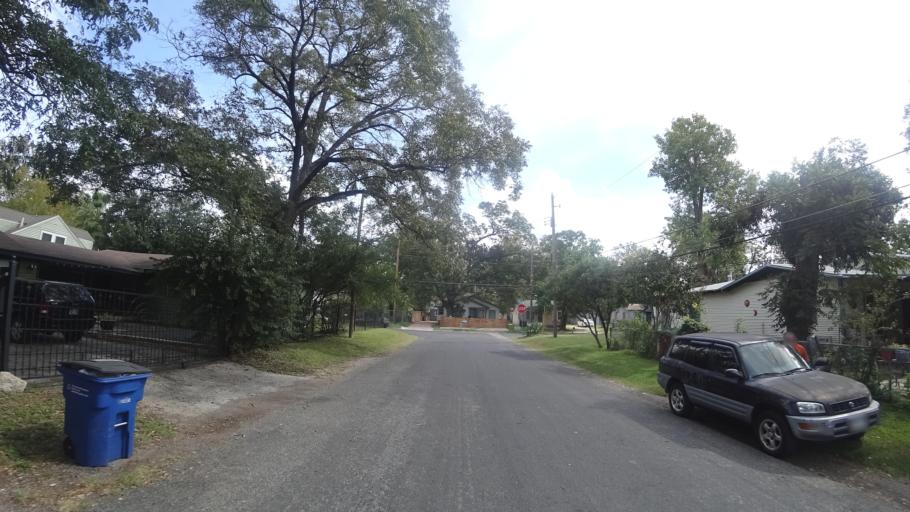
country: US
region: Texas
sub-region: Travis County
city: Austin
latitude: 30.2659
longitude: -97.6989
